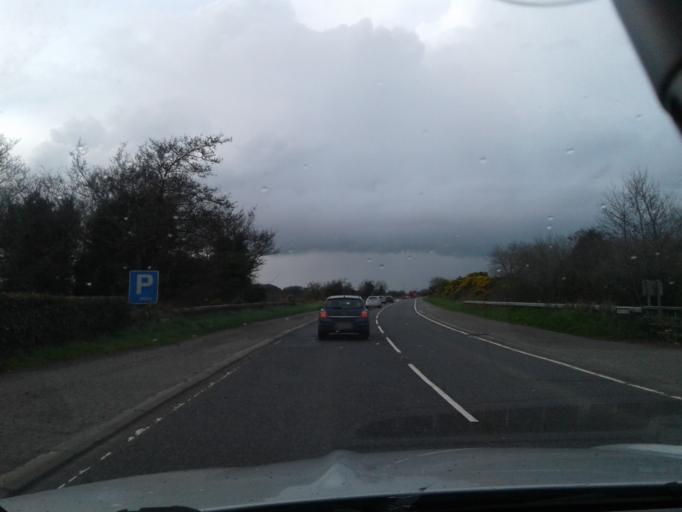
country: GB
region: Northern Ireland
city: Newtownstewart
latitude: 54.7363
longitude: -7.4325
